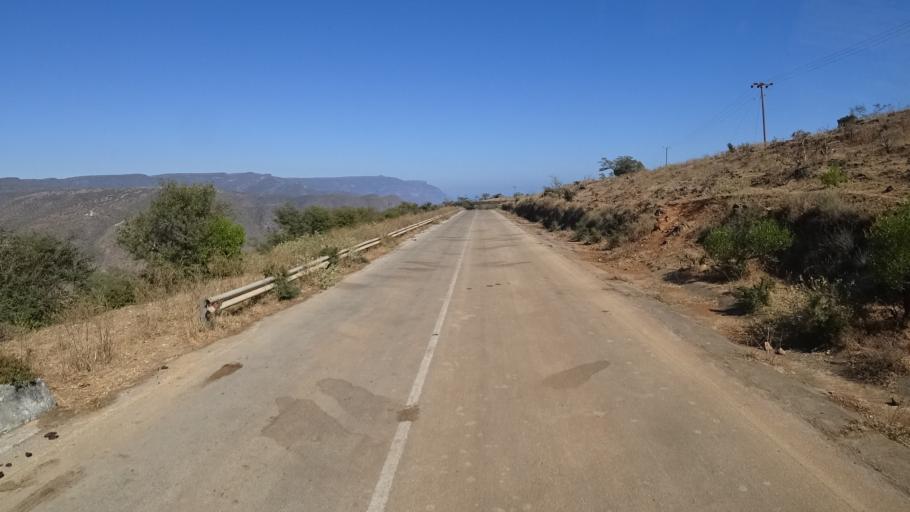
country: YE
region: Al Mahrah
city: Hawf
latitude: 16.7453
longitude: 53.3910
